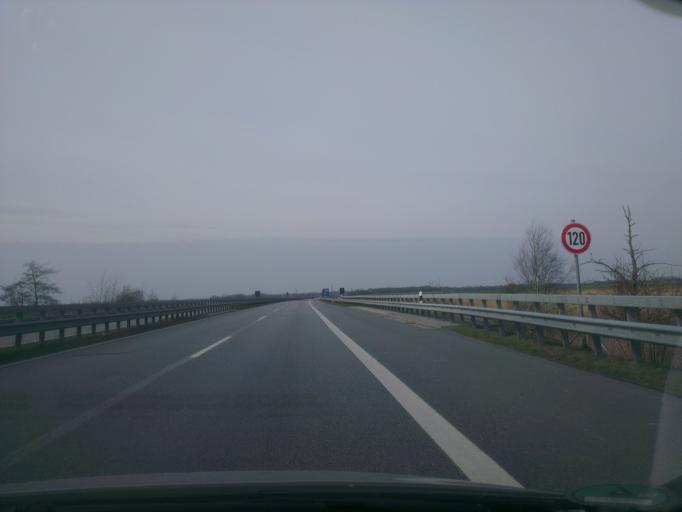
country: DE
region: Lower Saxony
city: Emden
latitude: 53.3646
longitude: 7.2658
